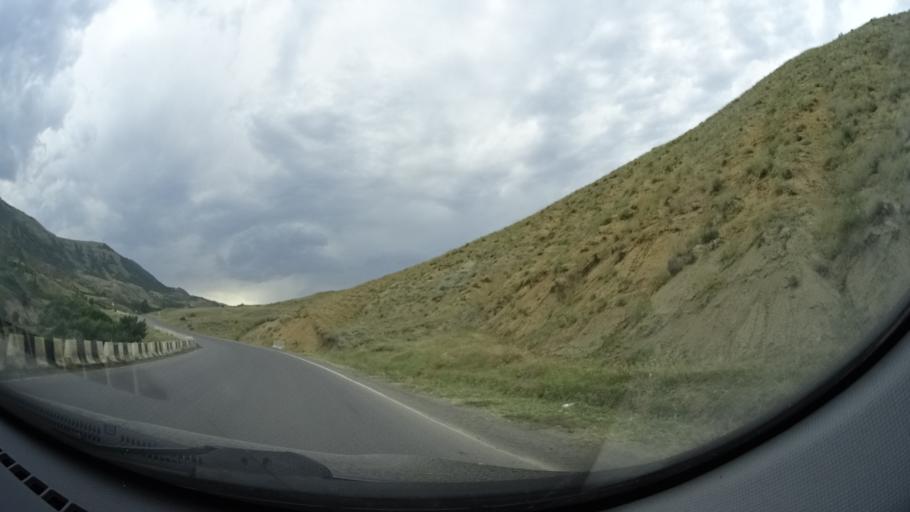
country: GE
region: Samtskhe-Javakheti
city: Aspindza
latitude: 41.5926
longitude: 43.1772
